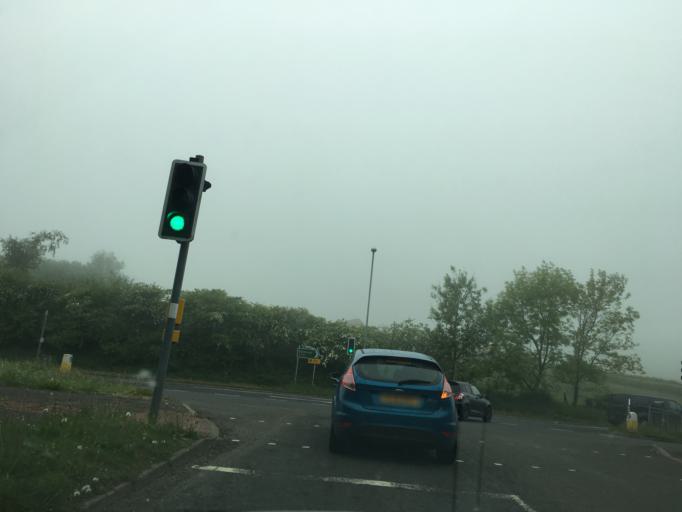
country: GB
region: Scotland
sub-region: Midlothian
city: Penicuik
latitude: 55.8523
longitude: -3.1906
